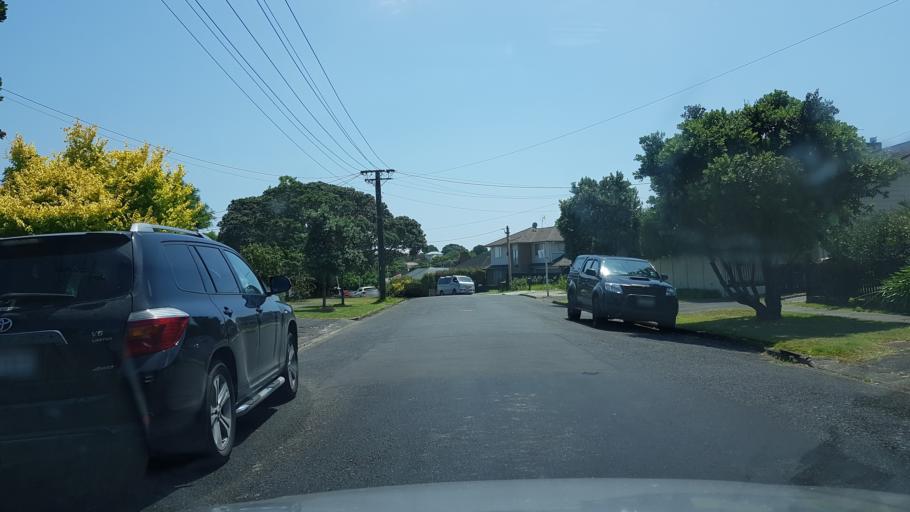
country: NZ
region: Auckland
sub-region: Auckland
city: North Shore
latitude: -36.8106
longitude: 174.7951
